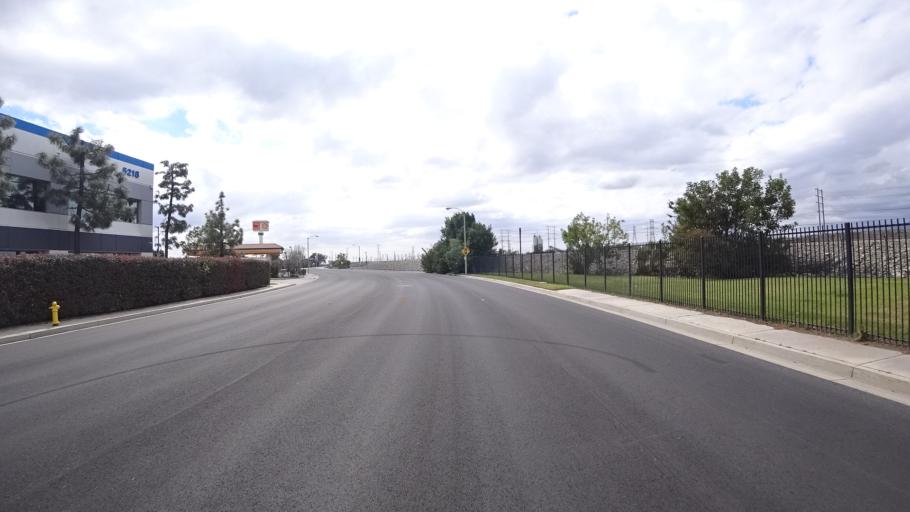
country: US
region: California
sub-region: Los Angeles County
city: Baldwin Park
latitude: 34.1082
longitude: -117.9729
